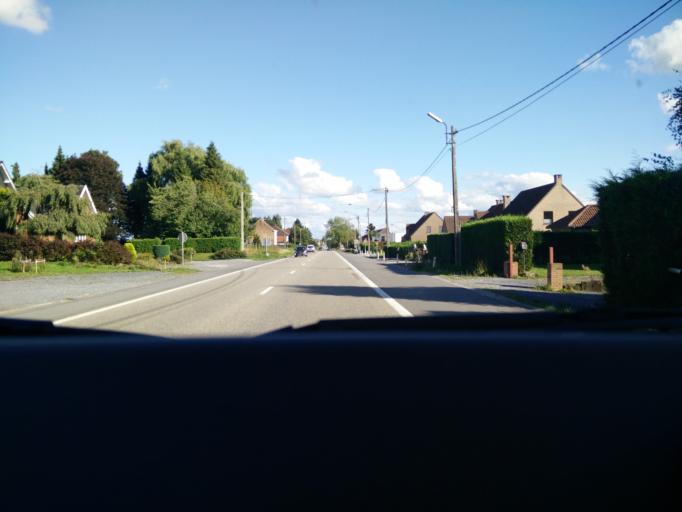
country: BE
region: Wallonia
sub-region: Province du Hainaut
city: Erquelinnes
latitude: 50.3211
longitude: 4.1197
